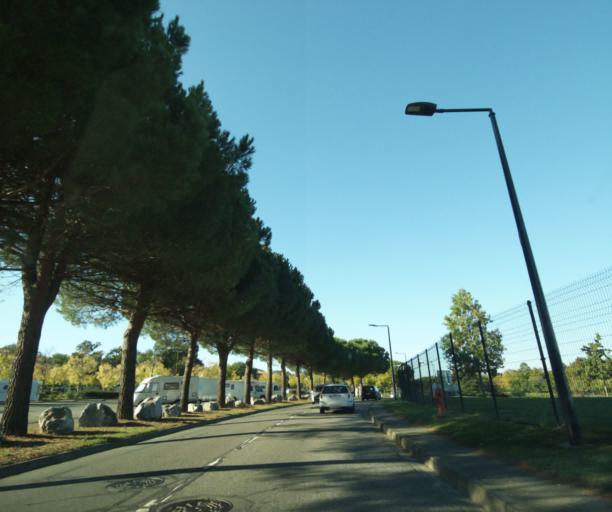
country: FR
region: Midi-Pyrenees
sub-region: Departement de la Haute-Garonne
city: Balma
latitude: 43.5861
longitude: 1.4911
